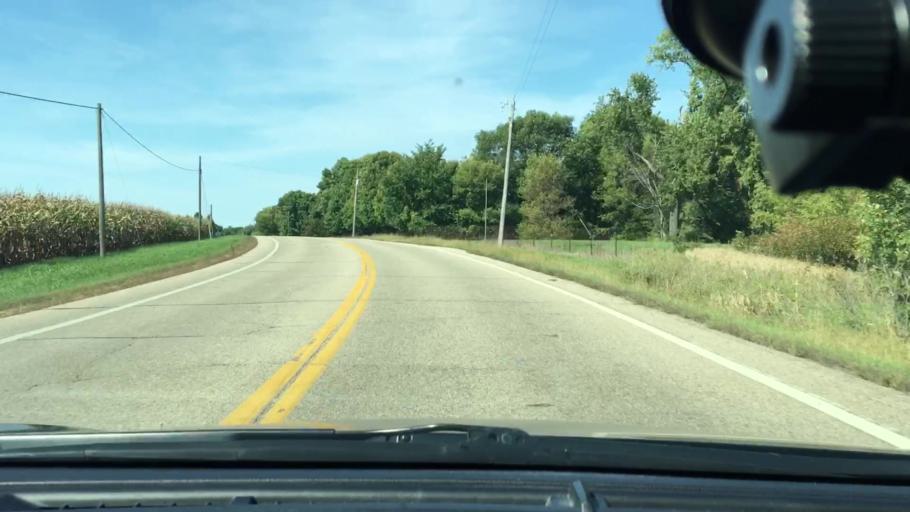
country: US
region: Minnesota
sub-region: Hennepin County
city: Corcoran
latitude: 45.1118
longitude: -93.5697
